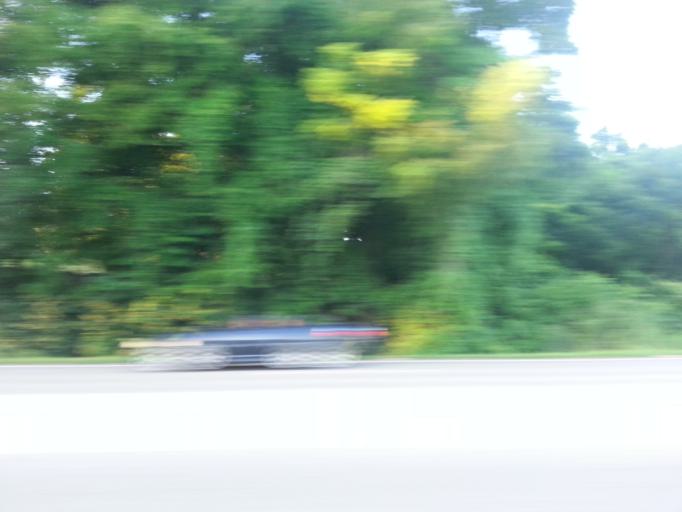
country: US
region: Tennessee
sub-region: Knox County
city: Farragut
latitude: 35.8666
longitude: -84.2007
